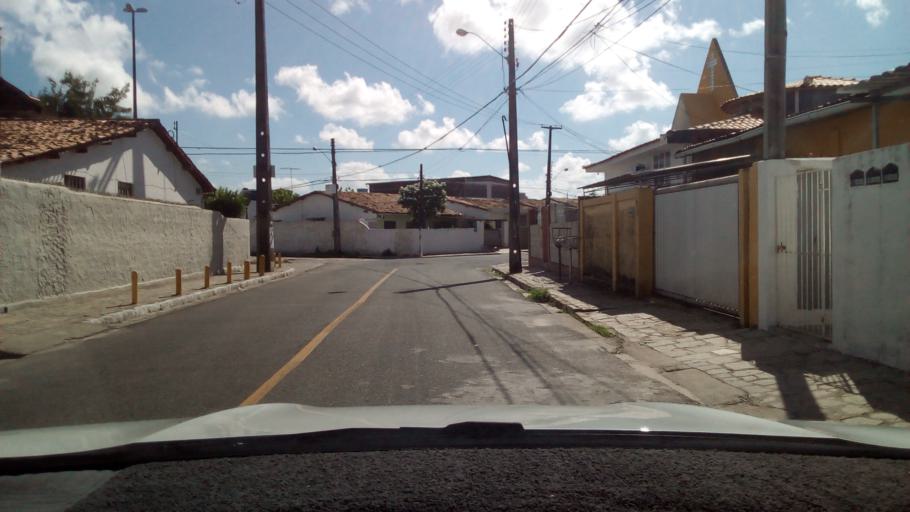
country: BR
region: Paraiba
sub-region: Joao Pessoa
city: Joao Pessoa
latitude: -7.1318
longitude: -34.8484
